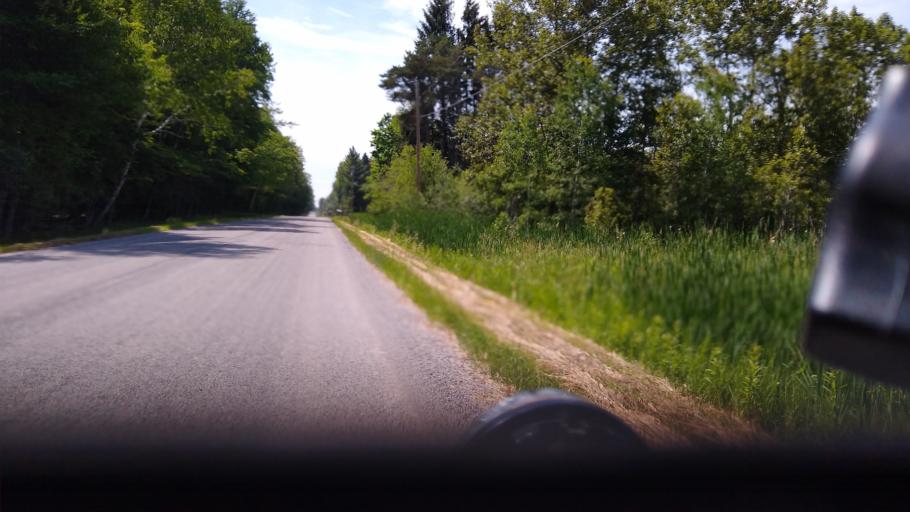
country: US
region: Michigan
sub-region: Delta County
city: Escanaba
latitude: 45.7101
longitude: -87.1374
